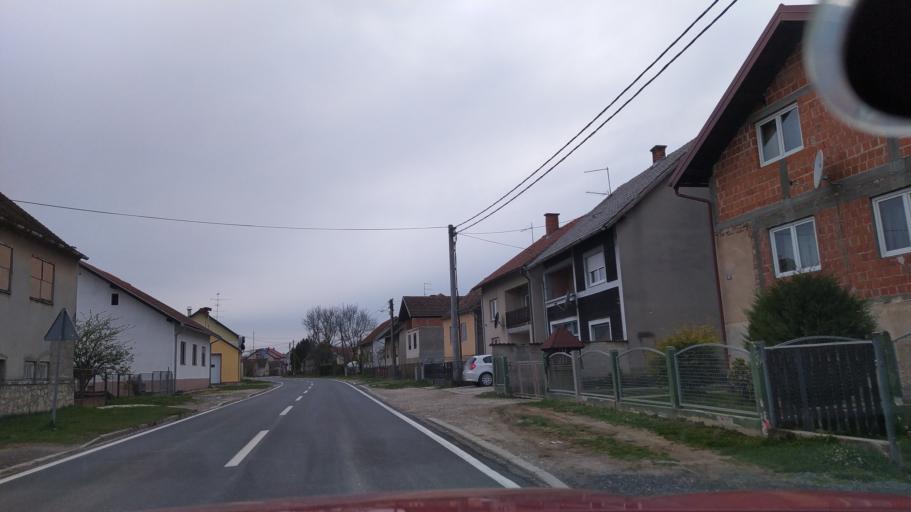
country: HR
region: Varazdinska
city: Jalzabet
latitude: 46.2096
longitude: 16.4563
